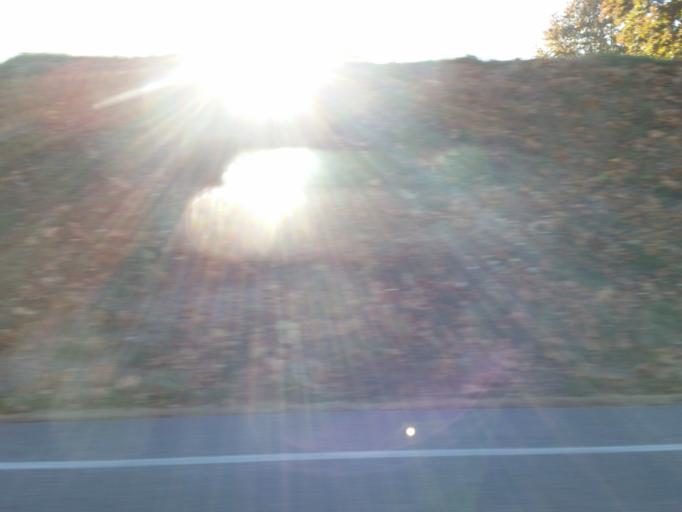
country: US
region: Pennsylvania
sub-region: Lebanon County
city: Annville
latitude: 40.3478
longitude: -76.5259
